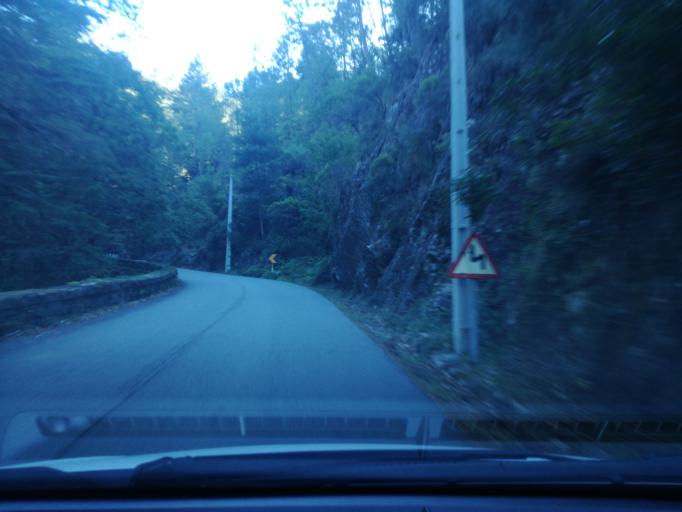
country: PT
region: Braga
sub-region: Vieira do Minho
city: Real
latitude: 41.7431
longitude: -8.1546
